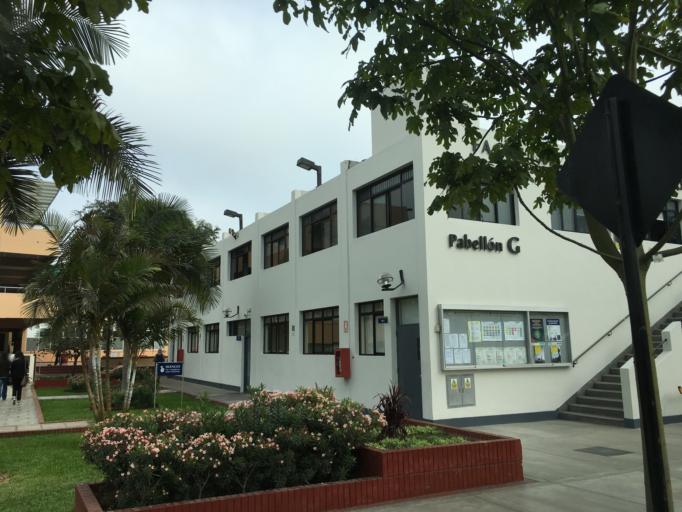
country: PE
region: Callao
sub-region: Callao
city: Callao
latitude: -12.0713
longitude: -77.0788
